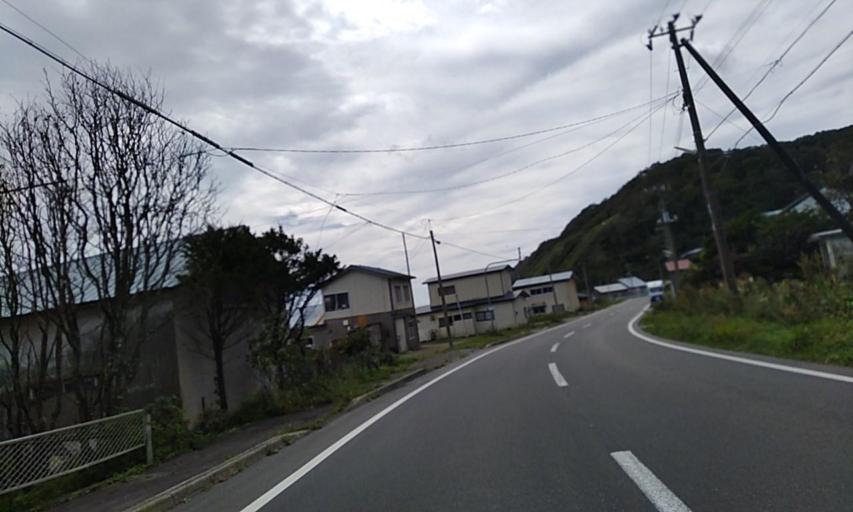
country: JP
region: Hokkaido
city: Kushiro
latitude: 42.7998
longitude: 143.8111
